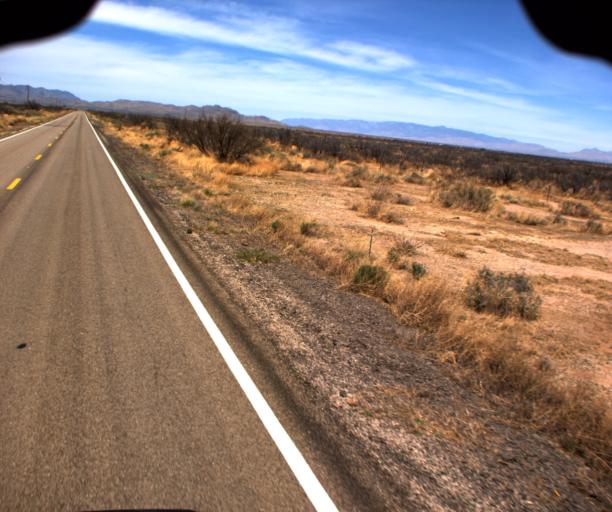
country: US
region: Arizona
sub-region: Cochise County
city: Willcox
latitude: 32.1615
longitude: -109.9418
